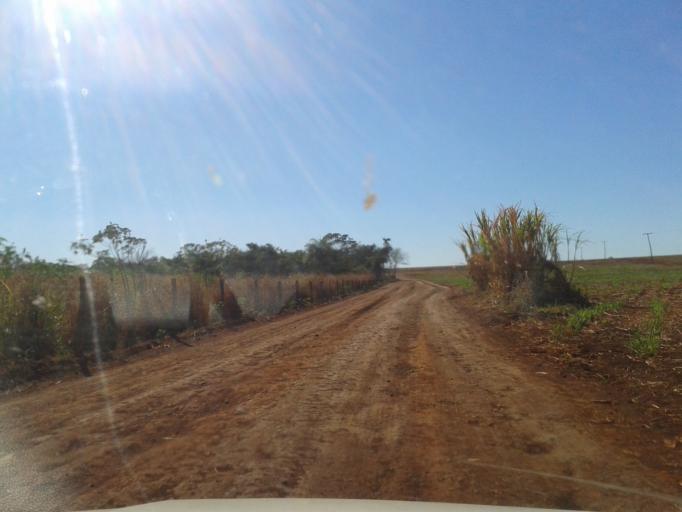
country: BR
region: Minas Gerais
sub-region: Centralina
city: Centralina
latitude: -18.5913
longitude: -49.1681
